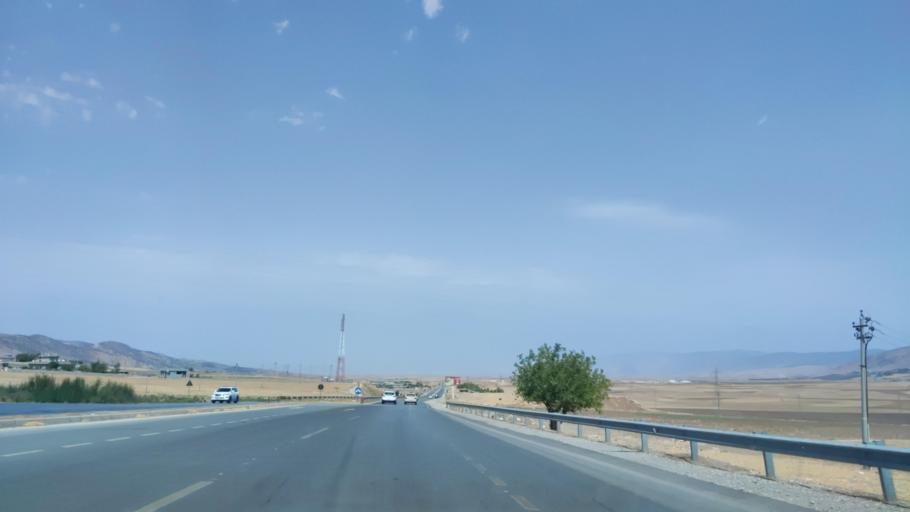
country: IQ
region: Arbil
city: Shaqlawah
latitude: 36.4933
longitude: 44.3695
